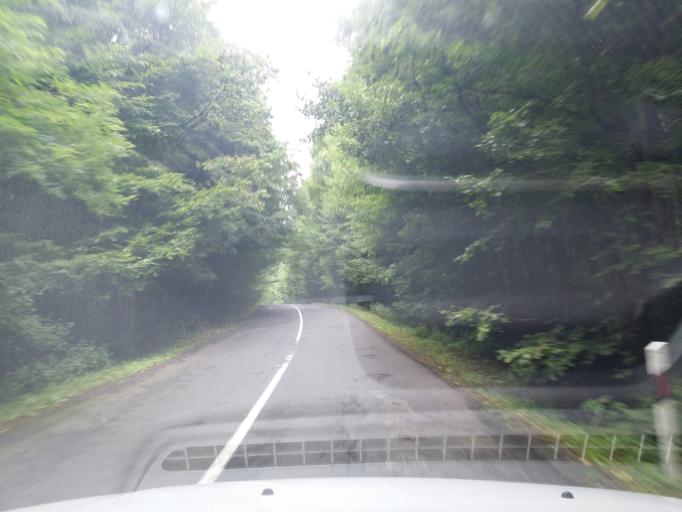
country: HU
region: Borsod-Abauj-Zemplen
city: Gonc
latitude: 48.4880
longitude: 21.4074
